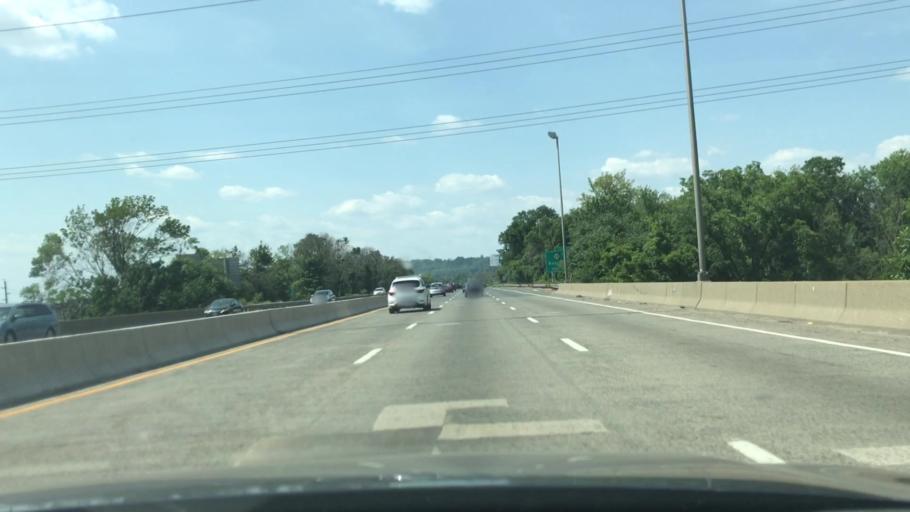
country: US
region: New Jersey
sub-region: Somerset County
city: South Bound Brook
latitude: 40.5560
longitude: -74.5456
